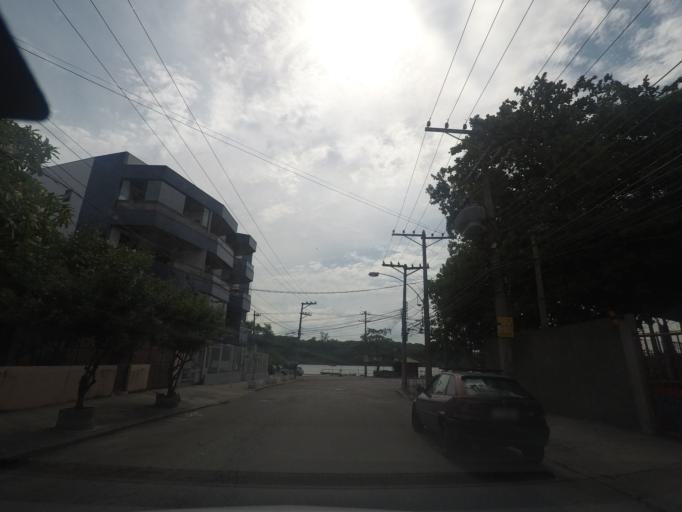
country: BR
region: Rio de Janeiro
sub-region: Rio De Janeiro
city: Rio de Janeiro
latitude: -22.8253
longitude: -43.1720
